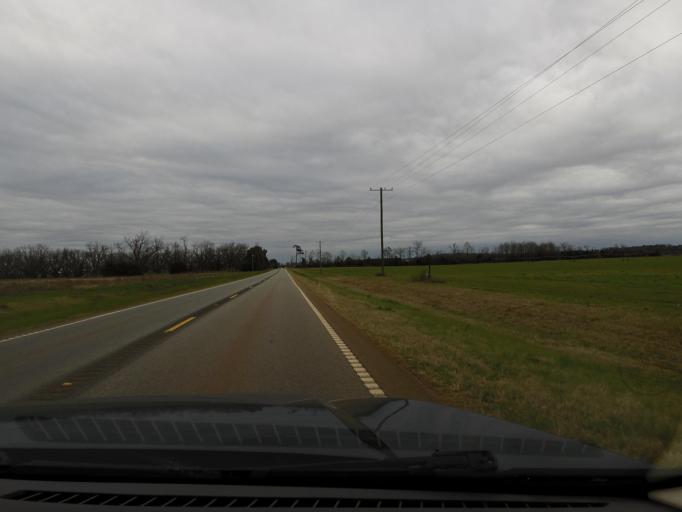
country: US
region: Georgia
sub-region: Randolph County
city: Shellman
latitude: 31.7723
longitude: -84.6372
